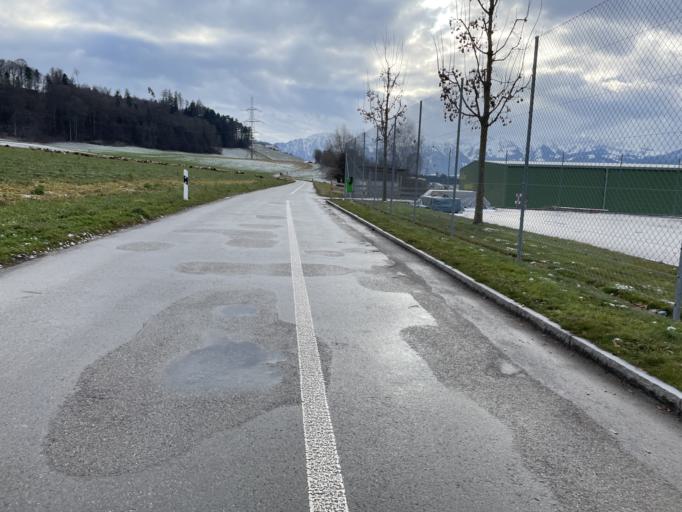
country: CH
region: Lucerne
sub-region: Entlebuch District
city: Oberdiessbach
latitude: 46.8318
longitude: 7.6172
